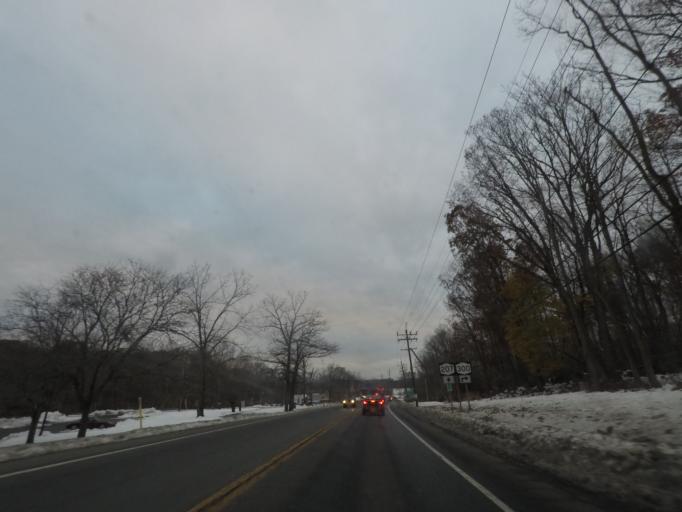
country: US
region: New York
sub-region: Orange County
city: Vails Gate
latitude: 41.4852
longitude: -74.0760
